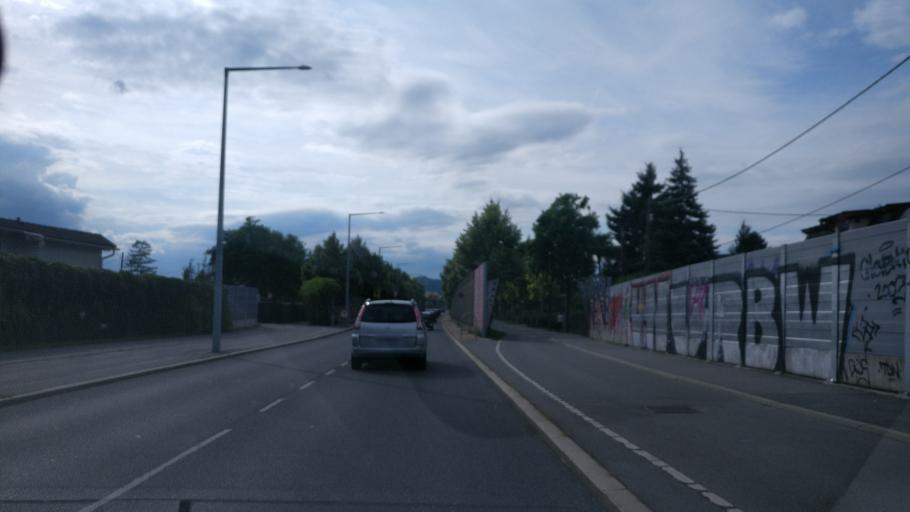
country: AT
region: Lower Austria
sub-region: Politischer Bezirk Wien-Umgebung
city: Gerasdorf bei Wien
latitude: 48.2571
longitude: 16.4196
